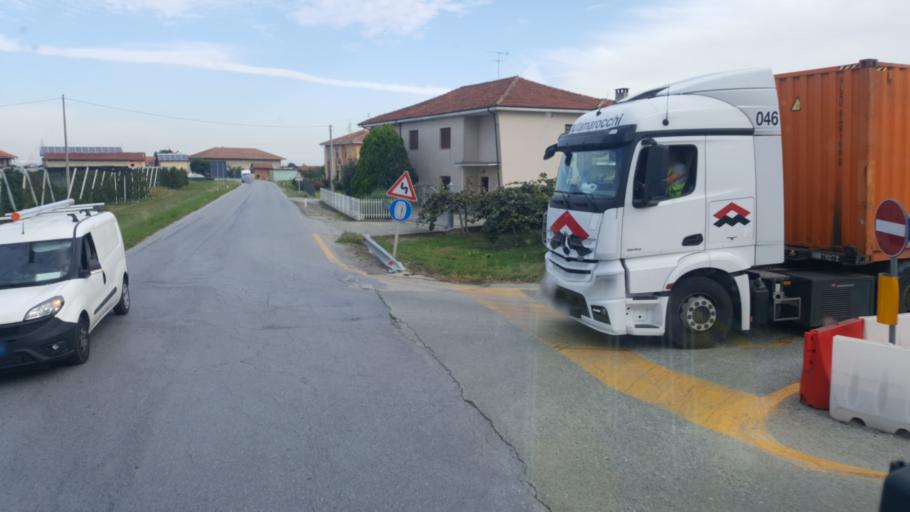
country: IT
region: Piedmont
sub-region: Provincia di Cuneo
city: Verzuolo
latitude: 44.5988
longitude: 7.4893
